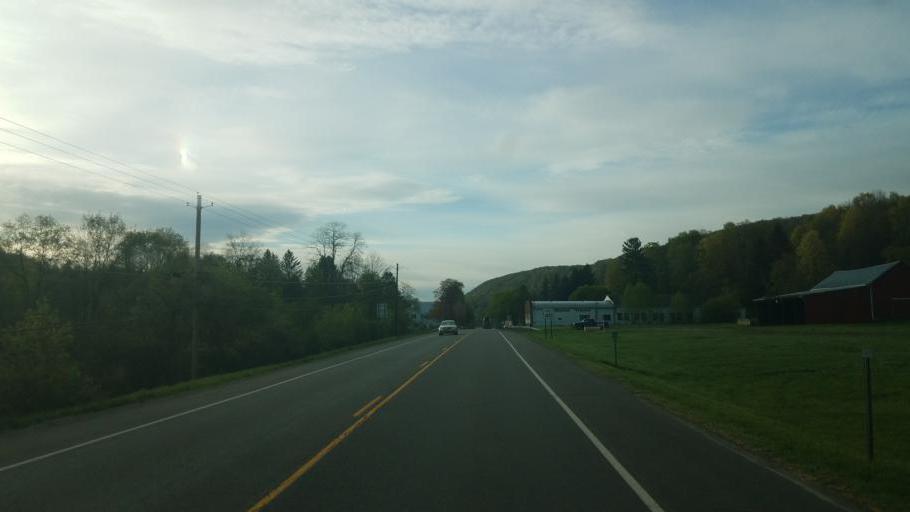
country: US
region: New York
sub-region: Steuben County
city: Hornell
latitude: 42.3388
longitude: -77.6910
